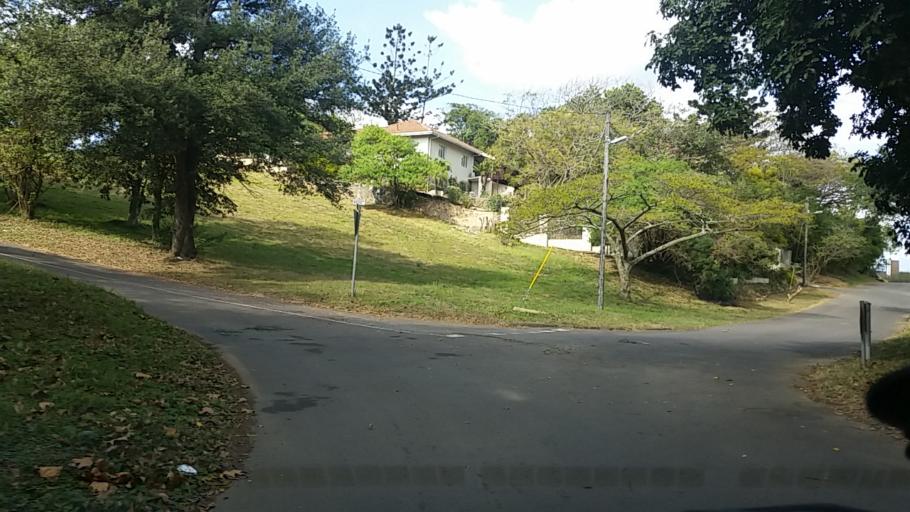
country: ZA
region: KwaZulu-Natal
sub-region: eThekwini Metropolitan Municipality
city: Berea
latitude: -29.8325
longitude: 30.9545
